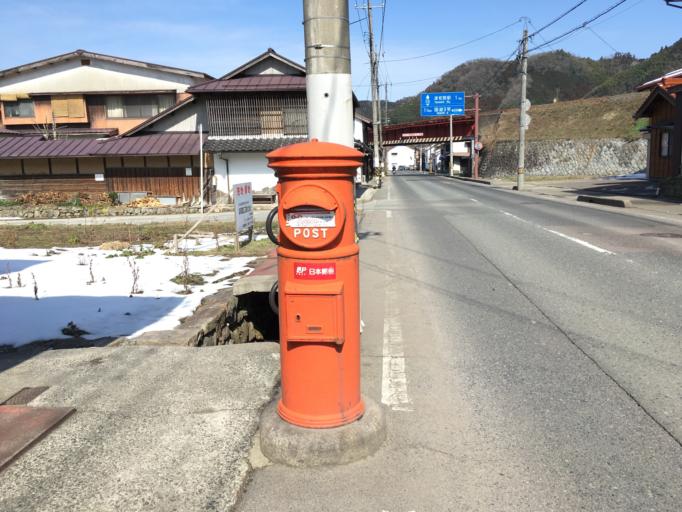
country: JP
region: Shimane
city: Masuda
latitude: 34.4635
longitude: 131.7724
